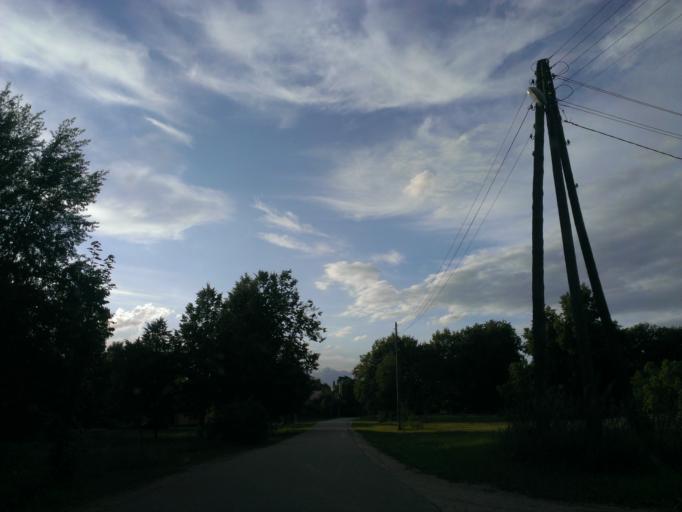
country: LV
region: Ikskile
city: Ikskile
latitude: 56.8404
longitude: 24.5054
